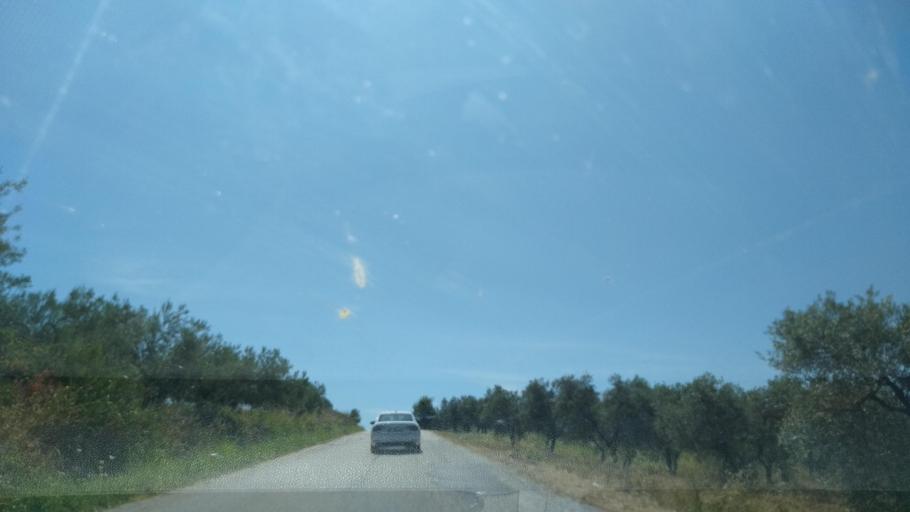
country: GR
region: Central Macedonia
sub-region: Nomos Chalkidikis
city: Agios Nikolaos
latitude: 40.3159
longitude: 23.6690
